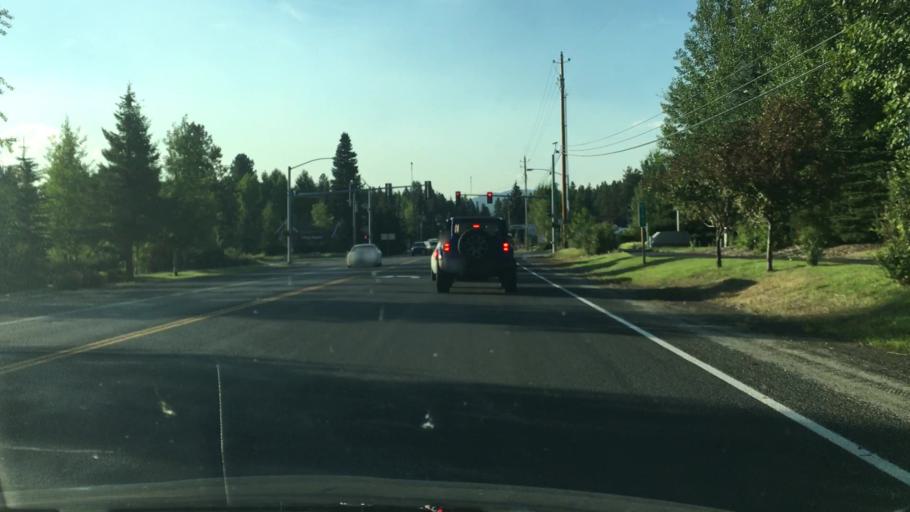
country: US
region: Idaho
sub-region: Valley County
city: McCall
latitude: 44.8970
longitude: -116.0962
